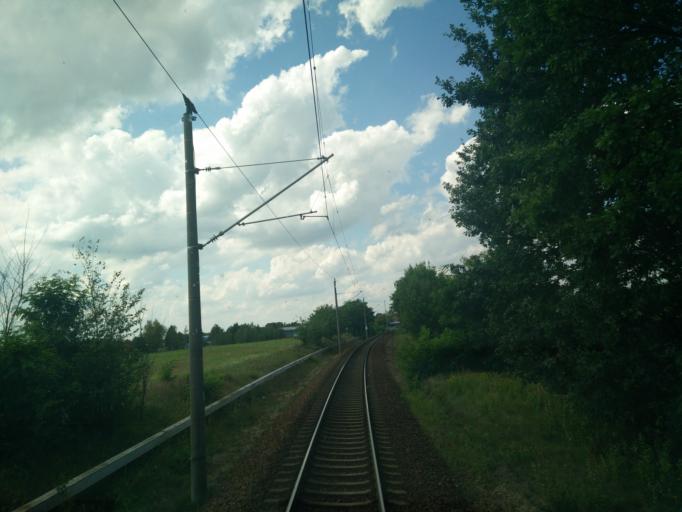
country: DE
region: Brandenburg
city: Vetschau
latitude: 51.7979
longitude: 14.0560
